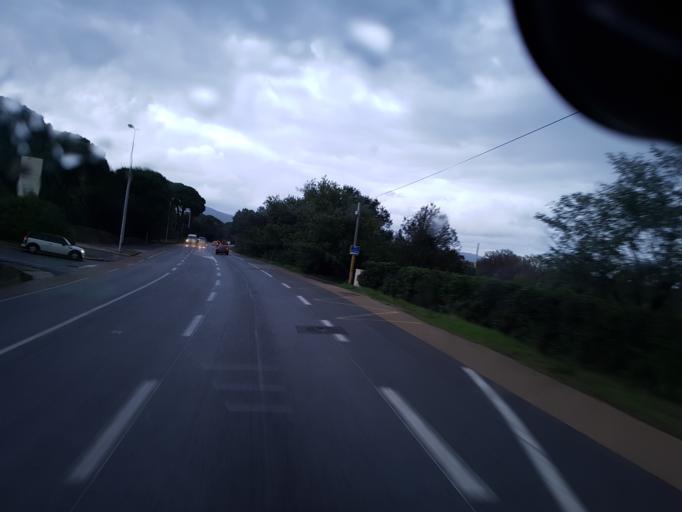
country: FR
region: Provence-Alpes-Cote d'Azur
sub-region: Departement du Var
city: Gassin
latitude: 43.2538
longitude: 6.5746
